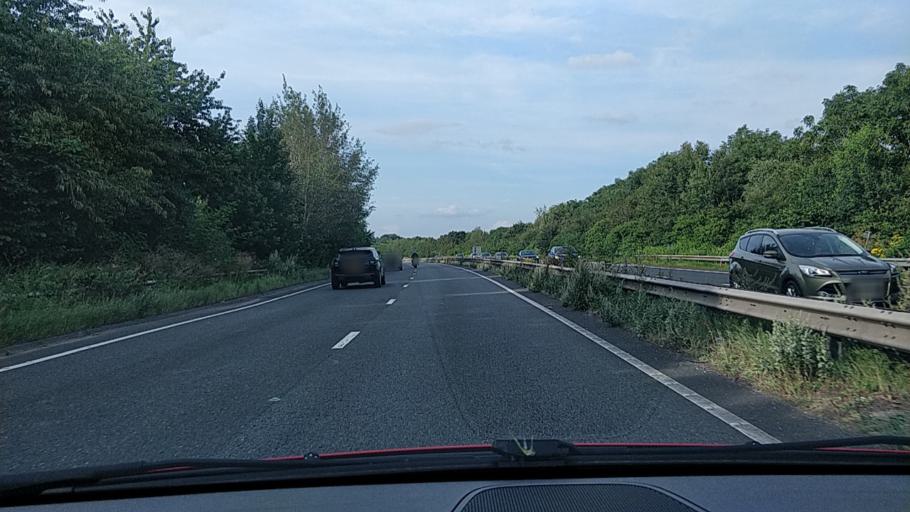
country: GB
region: England
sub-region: Cheshire West and Chester
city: Guilden Sutton
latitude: 53.1864
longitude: -2.8451
